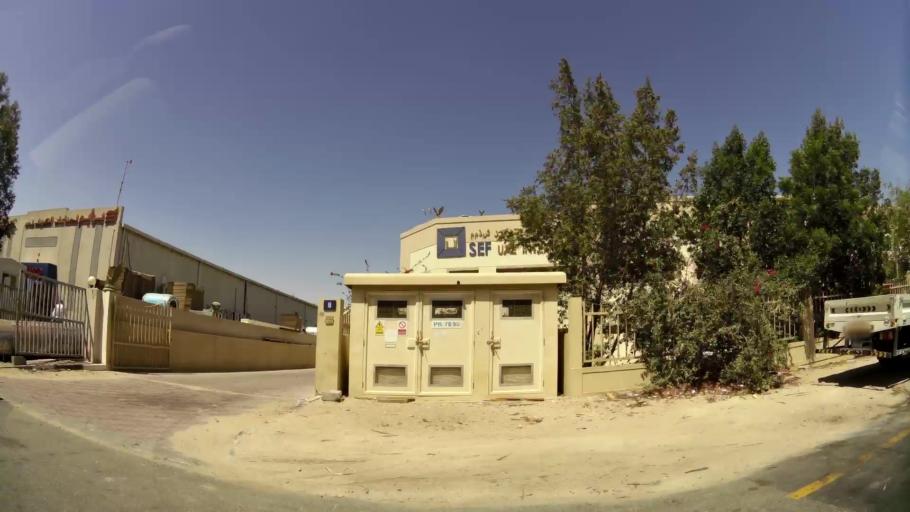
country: AE
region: Dubai
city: Dubai
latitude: 24.9794
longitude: 55.2063
